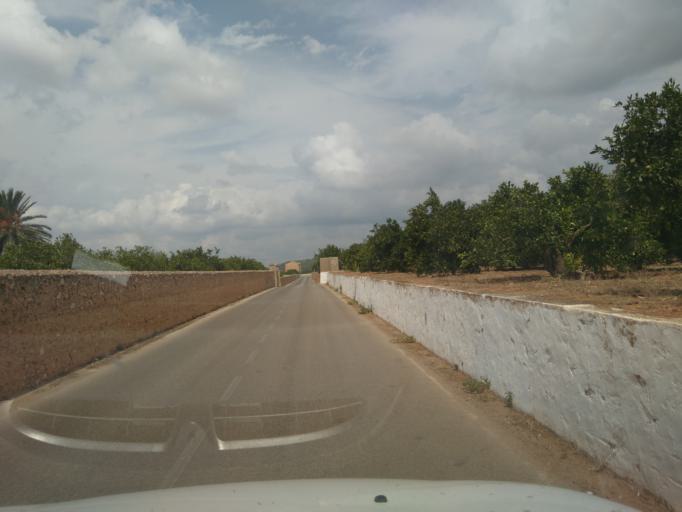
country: ES
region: Valencia
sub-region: Provincia de Valencia
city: La Pobla Llarga
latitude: 39.0945
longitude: -0.4300
